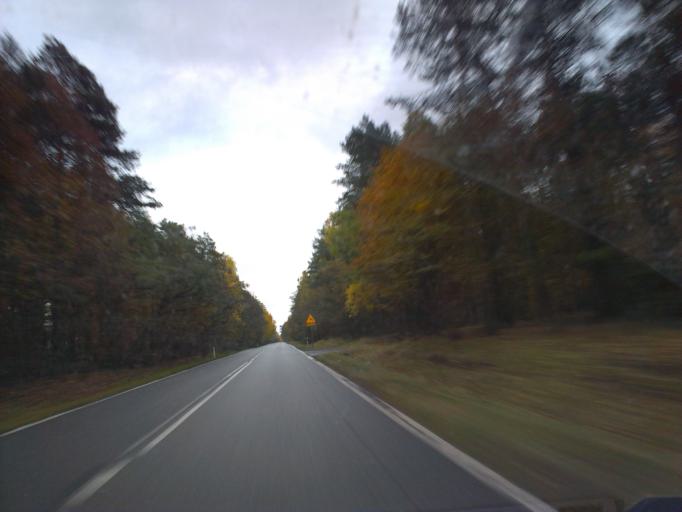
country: PL
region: Kujawsko-Pomorskie
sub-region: Powiat swiecki
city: Lniano
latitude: 53.4724
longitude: 18.1587
